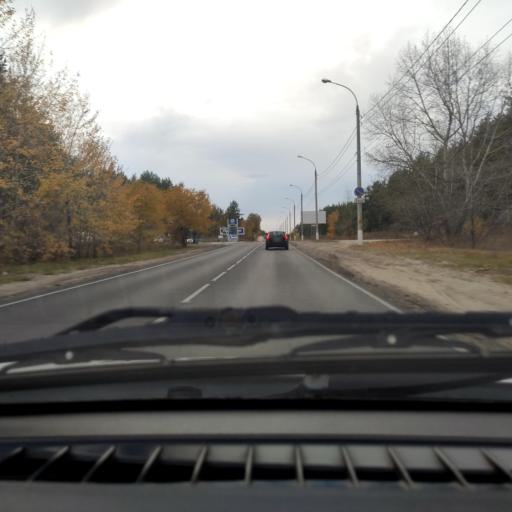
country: RU
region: Samara
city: Zhigulevsk
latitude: 53.4771
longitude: 49.4505
